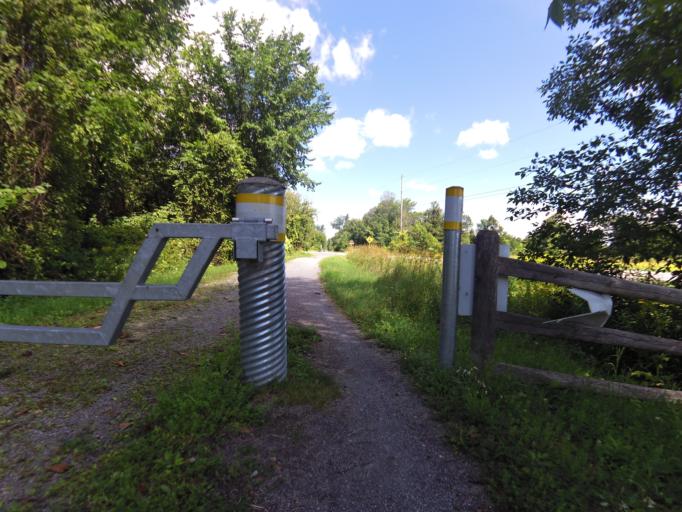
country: CA
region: Ontario
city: Ottawa
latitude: 45.2735
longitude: -75.6245
